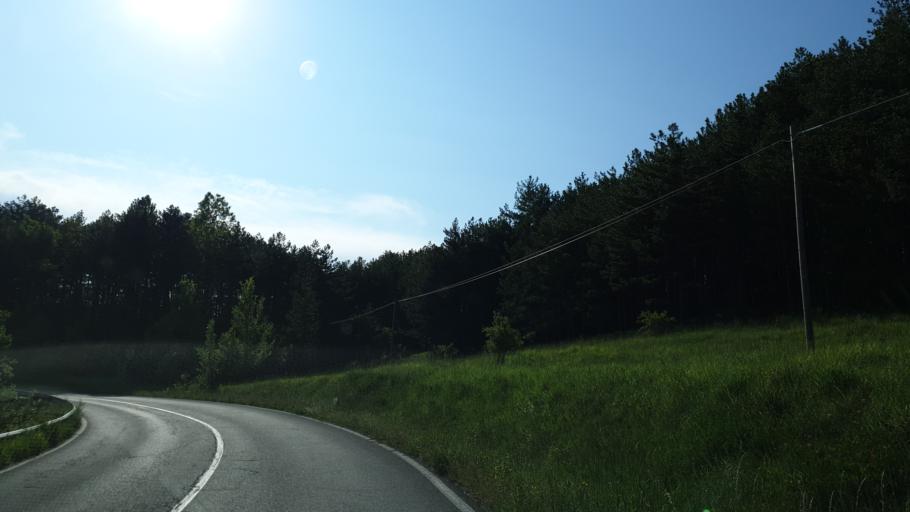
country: IT
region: Tuscany
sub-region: Province of Arezzo
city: Montemignaio
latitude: 43.7875
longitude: 11.6452
